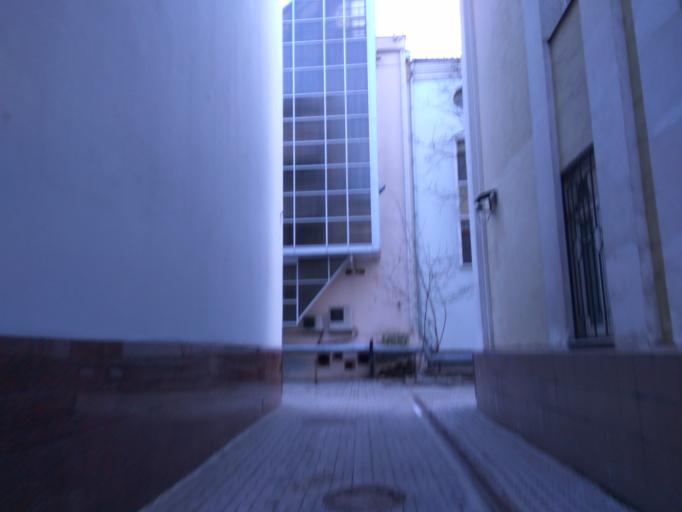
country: RU
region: Moscow
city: Moscow
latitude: 55.7698
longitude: 37.6289
